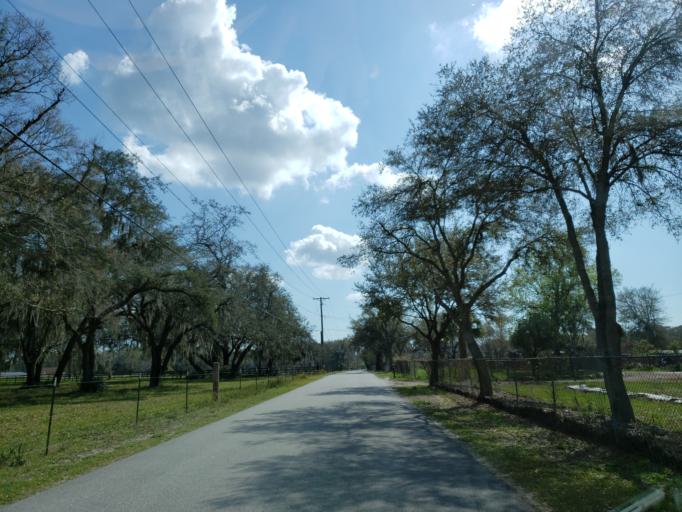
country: US
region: Florida
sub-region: Hillsborough County
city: Keystone
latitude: 28.1466
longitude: -82.6409
